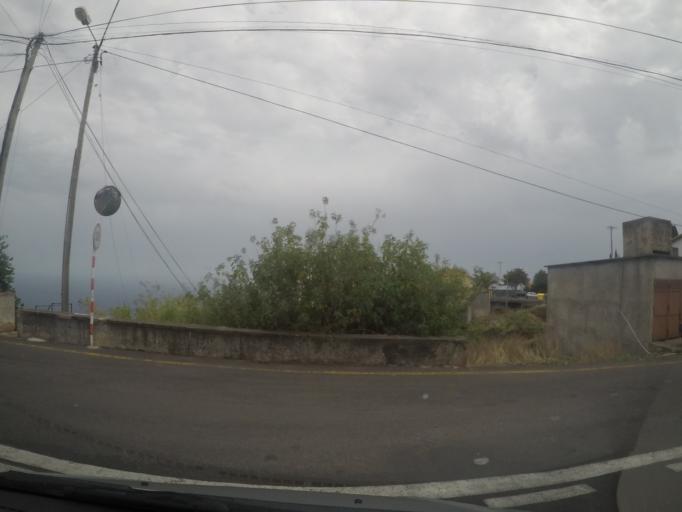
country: PT
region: Madeira
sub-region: Santa Cruz
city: Santa Cruz
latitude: 32.6744
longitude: -16.8106
